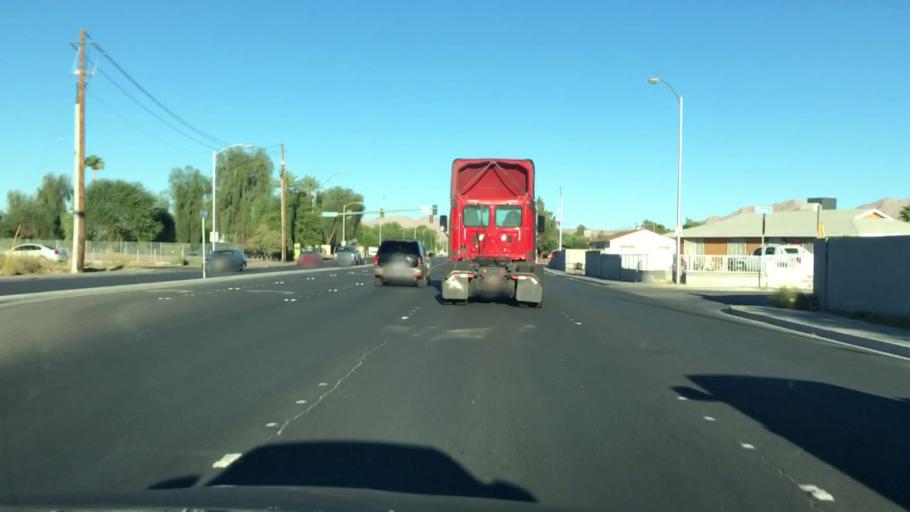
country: US
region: Nevada
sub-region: Clark County
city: North Las Vegas
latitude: 36.2176
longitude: -115.1085
